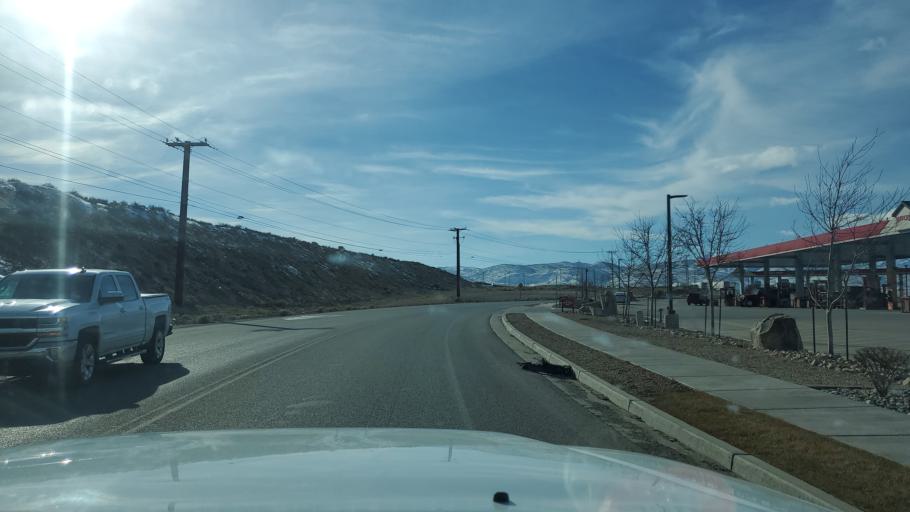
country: US
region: Utah
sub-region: Salt Lake County
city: Bluffdale
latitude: 40.4820
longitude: -111.8970
